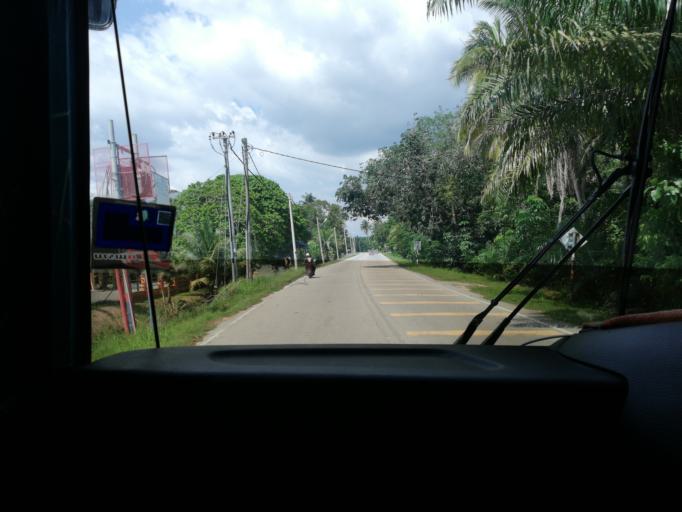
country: MY
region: Perak
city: Parit Buntar
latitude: 5.1164
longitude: 100.5596
